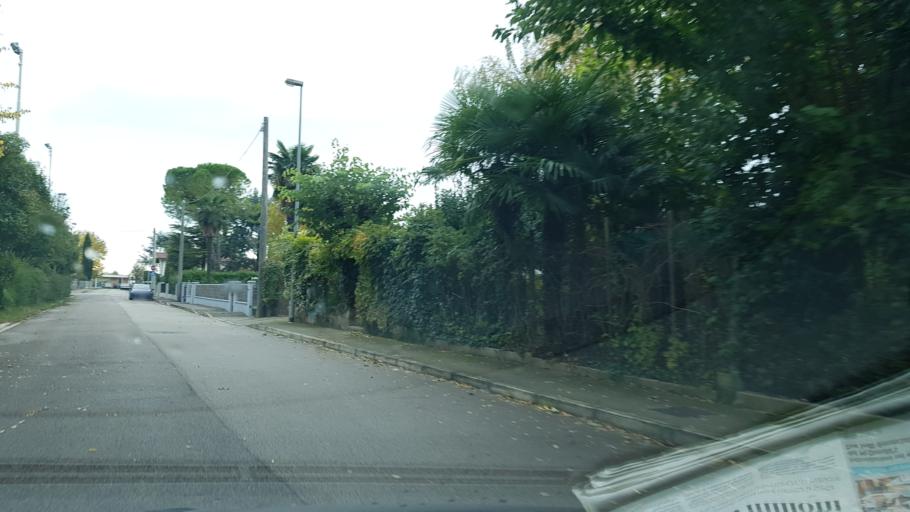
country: IT
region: Friuli Venezia Giulia
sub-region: Provincia di Gorizia
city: San Pier d'Isonzo
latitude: 45.8462
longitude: 13.4591
